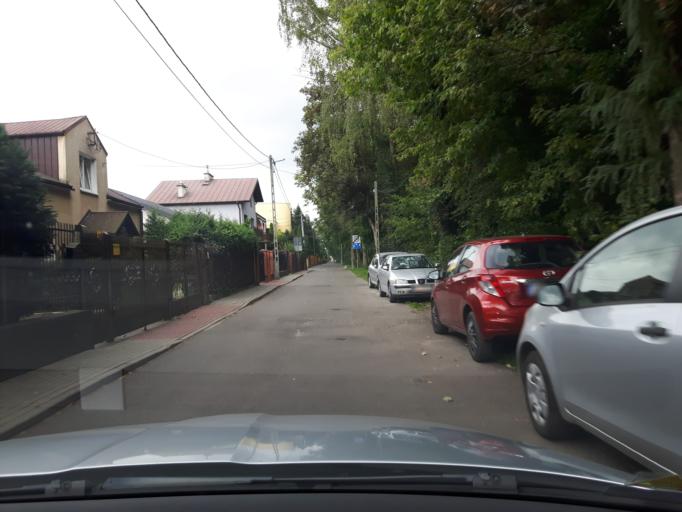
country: PL
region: Masovian Voivodeship
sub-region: Warszawa
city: Praga Poludnie
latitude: 52.2492
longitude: 21.1250
